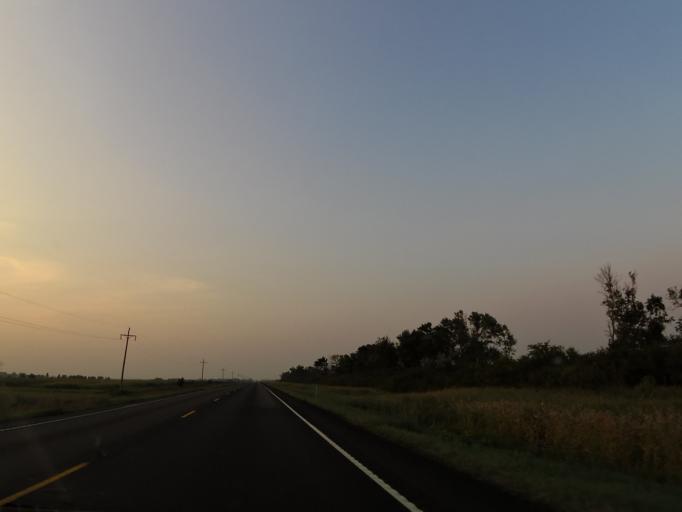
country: US
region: North Dakota
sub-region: Walsh County
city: Park River
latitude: 48.2383
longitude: -97.6225
